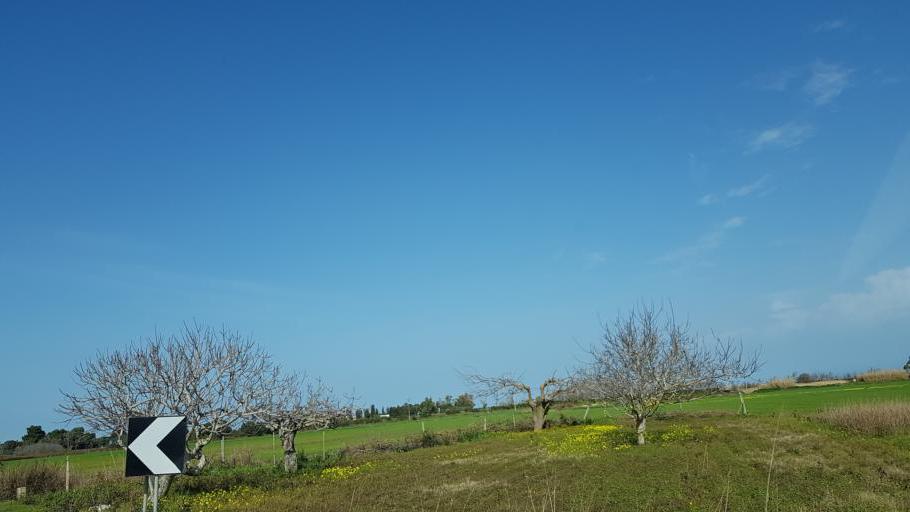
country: IT
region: Apulia
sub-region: Provincia di Brindisi
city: Brindisi
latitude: 40.6523
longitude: 17.9080
